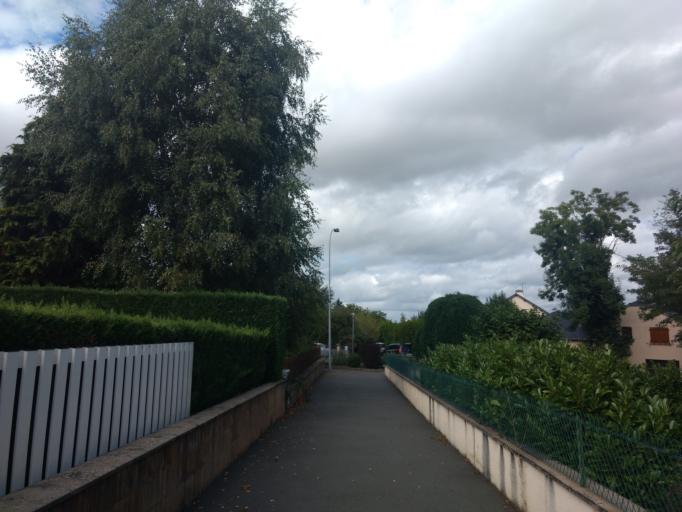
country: FR
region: Midi-Pyrenees
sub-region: Departement de l'Aveyron
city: Colombies
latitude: 44.4066
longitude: 2.2965
